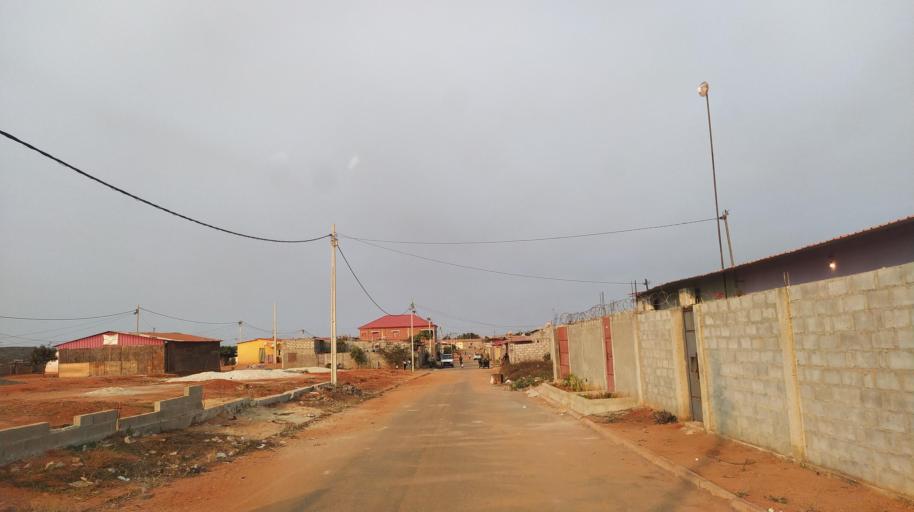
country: AO
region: Luanda
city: Luanda
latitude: -9.0736
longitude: 13.4260
